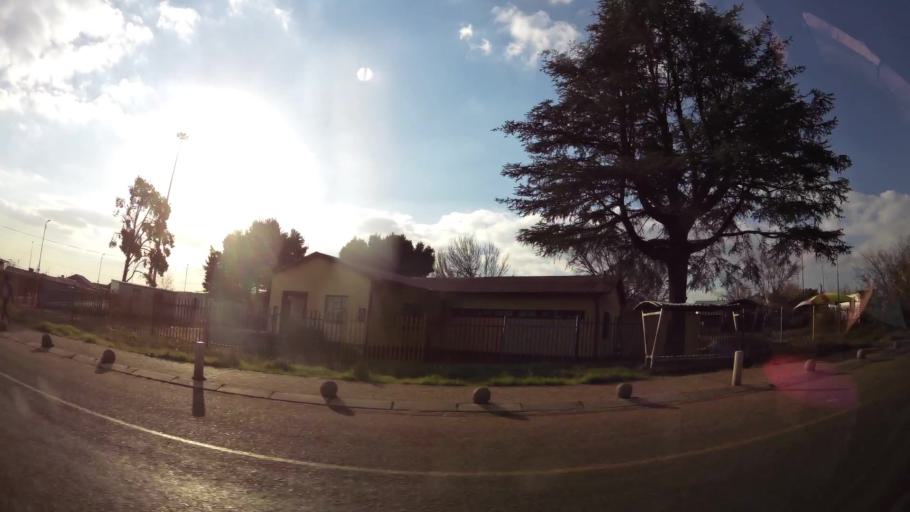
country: ZA
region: Gauteng
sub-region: West Rand District Municipality
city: Krugersdorp
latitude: -26.0819
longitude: 27.7580
